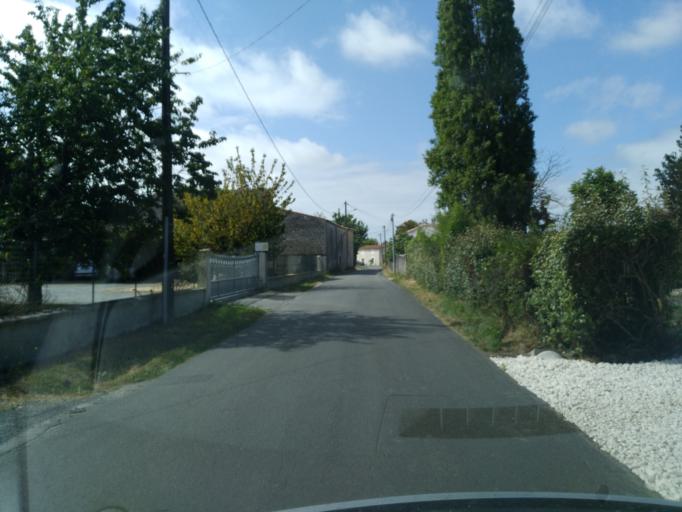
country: FR
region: Poitou-Charentes
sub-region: Departement de la Charente-Maritime
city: Breuillet
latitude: 45.6903
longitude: -1.0706
